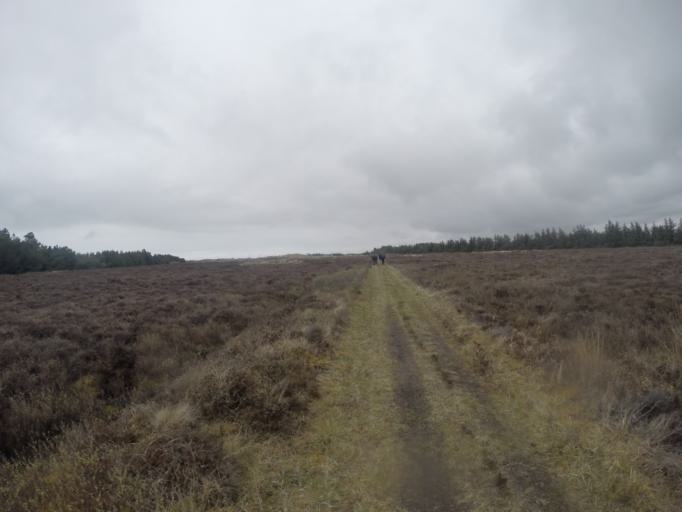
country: DK
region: North Denmark
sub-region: Thisted Kommune
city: Hurup
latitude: 56.9115
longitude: 8.3513
